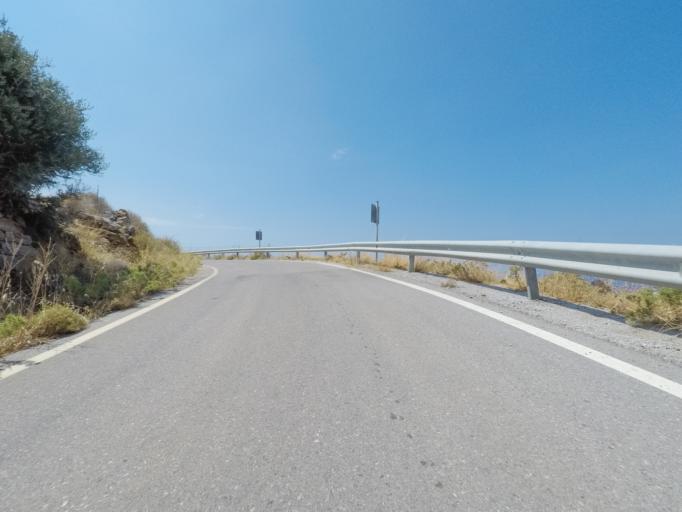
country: GR
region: Crete
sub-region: Nomos Lasithiou
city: Elounda
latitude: 35.3178
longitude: 25.6786
